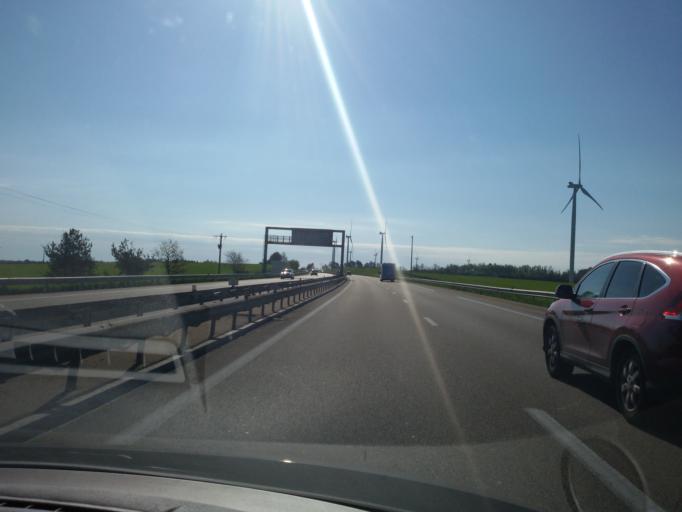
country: FR
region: Bourgogne
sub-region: Departement de l'Yonne
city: Saint-Bris-le-Vineux
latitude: 47.7791
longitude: 3.6878
